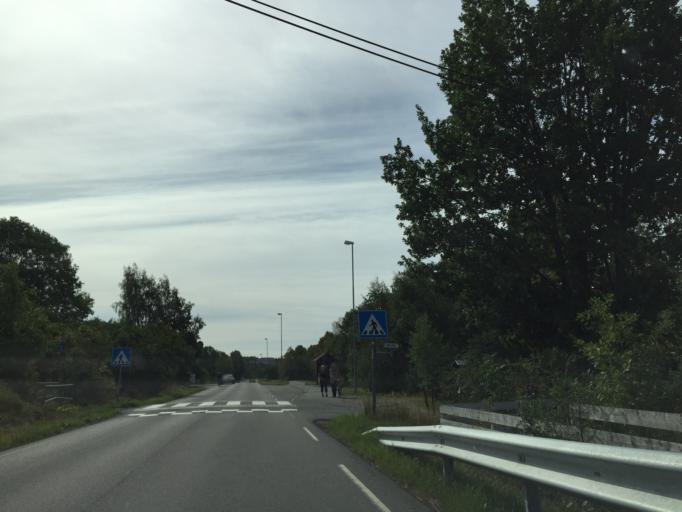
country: NO
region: Ostfold
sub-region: Moss
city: Moss
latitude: 59.5007
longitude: 10.6859
